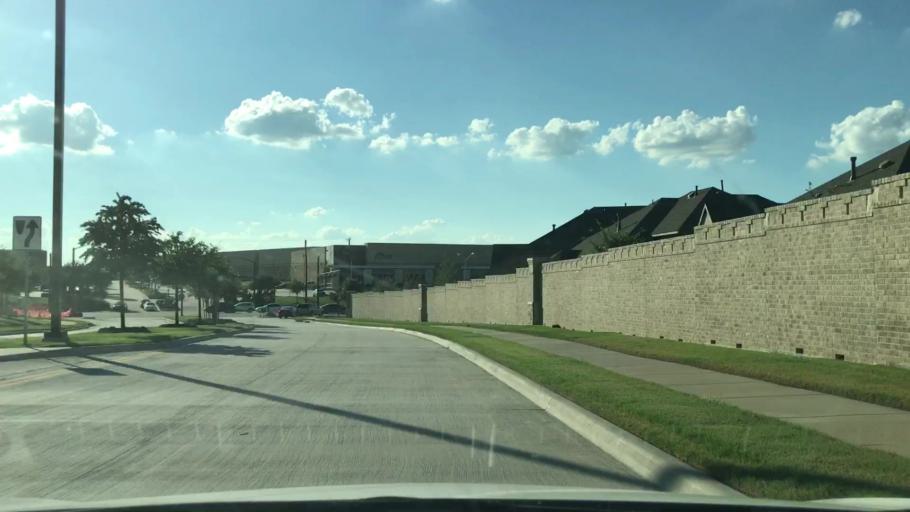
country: US
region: Texas
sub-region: Dallas County
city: Coppell
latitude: 32.8996
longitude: -96.9896
